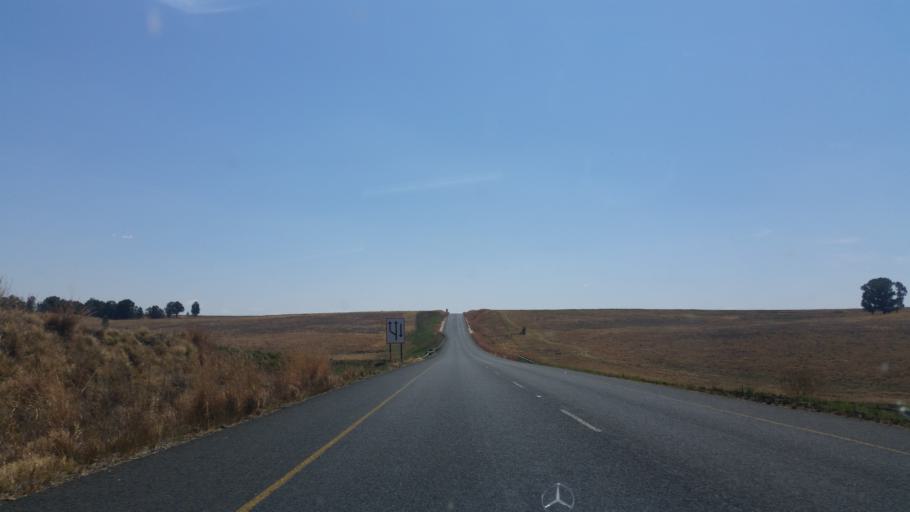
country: ZA
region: Orange Free State
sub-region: Thabo Mofutsanyana District Municipality
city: Phuthaditjhaba
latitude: -28.1768
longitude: 28.6847
